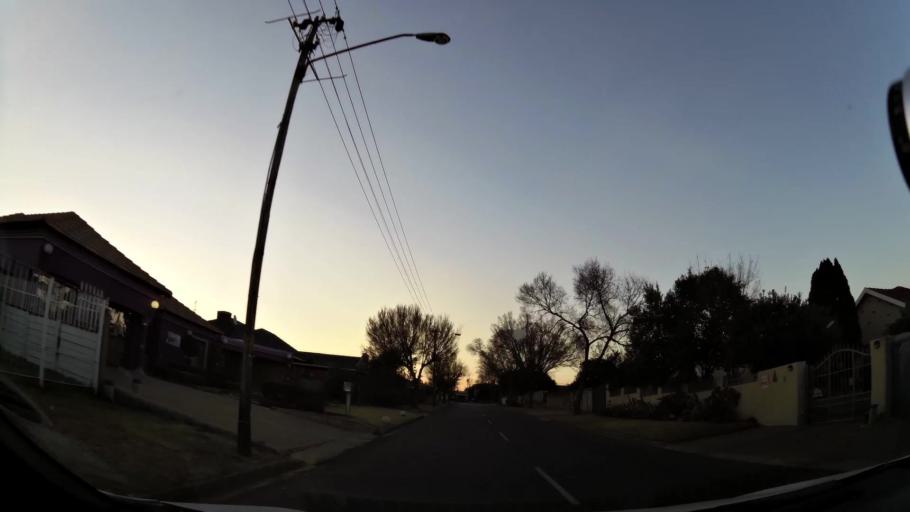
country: ZA
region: Gauteng
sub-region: Ekurhuleni Metropolitan Municipality
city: Germiston
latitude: -26.2613
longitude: 28.1612
